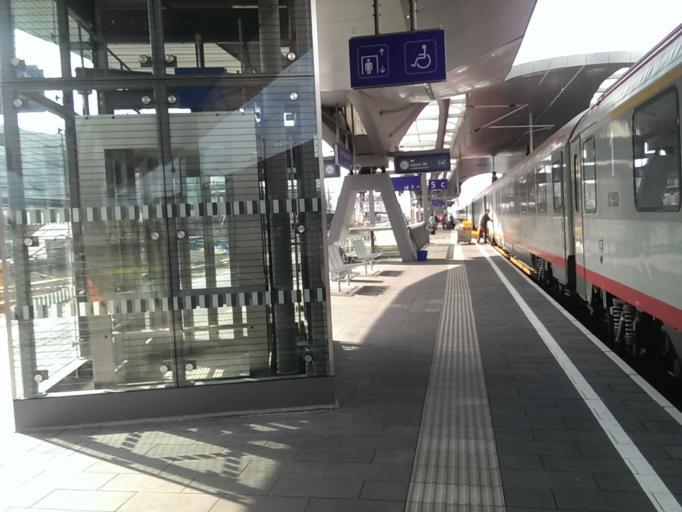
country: AT
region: Styria
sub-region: Graz Stadt
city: Wetzelsdorf
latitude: 47.0733
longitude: 15.4163
